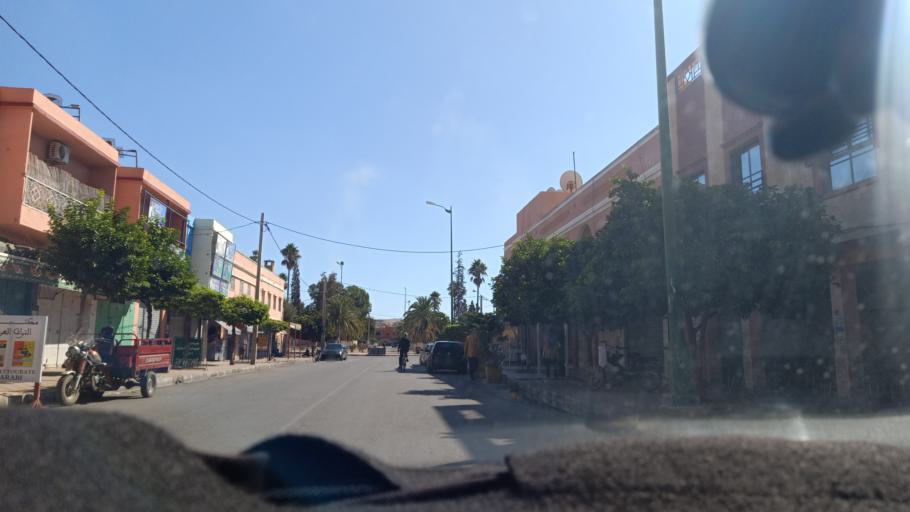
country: MA
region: Doukkala-Abda
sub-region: Safi
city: Youssoufia
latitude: 32.2459
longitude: -8.5335
